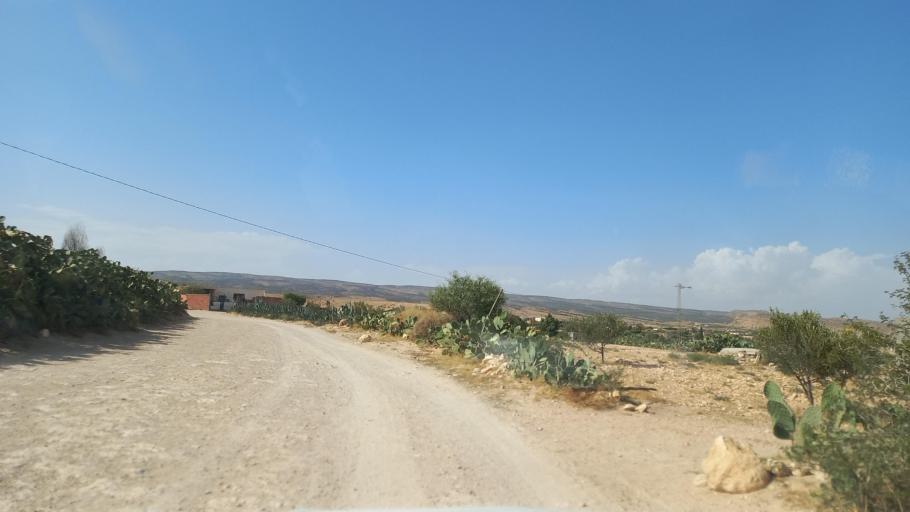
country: TN
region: Al Qasrayn
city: Kasserine
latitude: 35.2756
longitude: 8.9447
